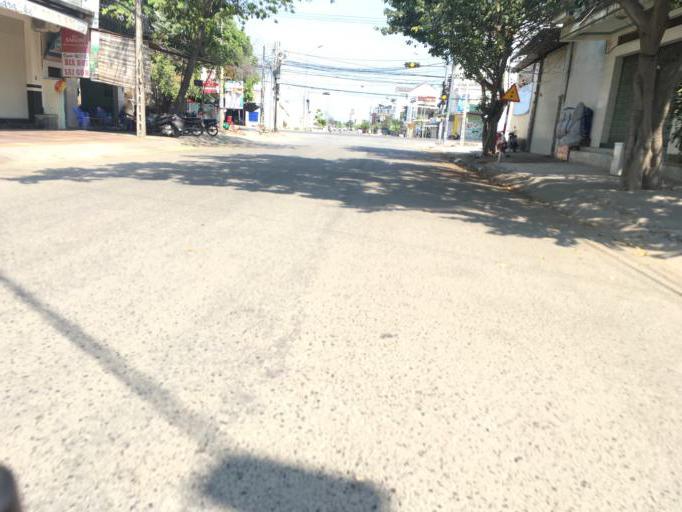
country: VN
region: Ninh Thuan
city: Phan Rang-Thap Cham
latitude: 11.5701
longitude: 108.9941
